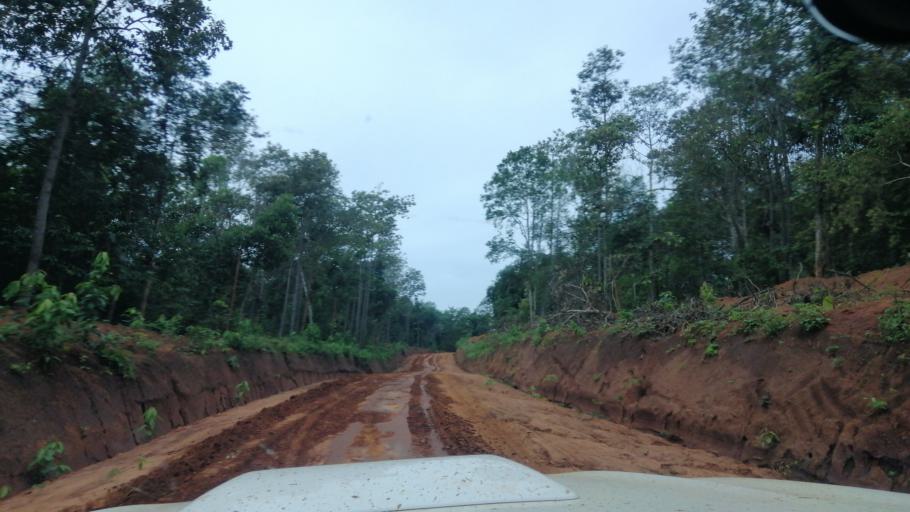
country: TH
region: Loei
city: Na Haeo
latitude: 17.5785
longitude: 101.1690
